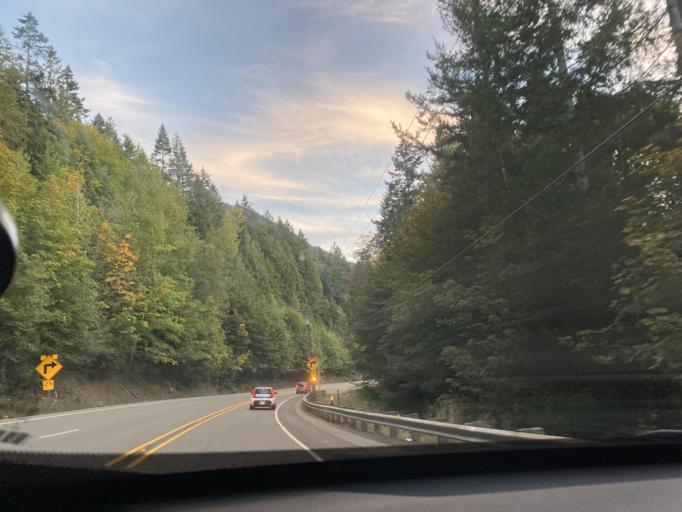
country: US
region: Washington
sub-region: Clallam County
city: Port Angeles
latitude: 48.0679
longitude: -123.5757
